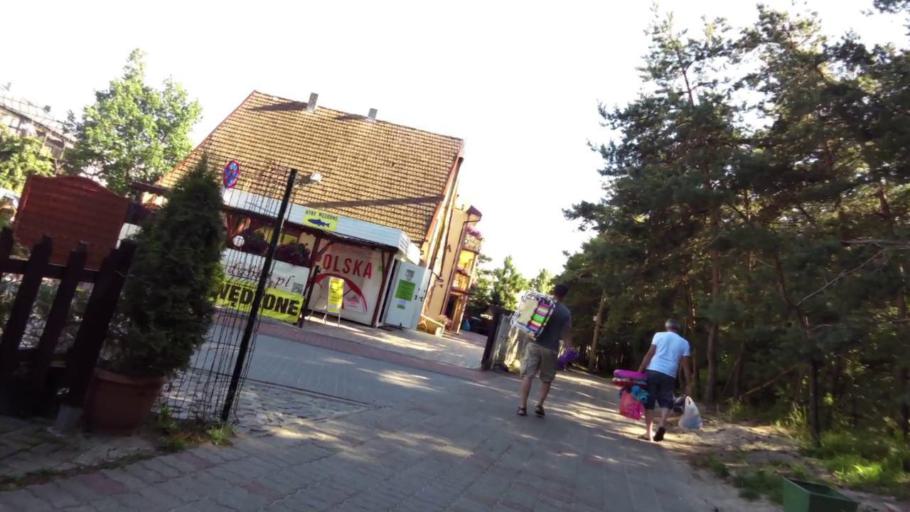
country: PL
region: West Pomeranian Voivodeship
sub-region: Powiat slawienski
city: Darlowo
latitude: 54.3807
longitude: 16.3128
